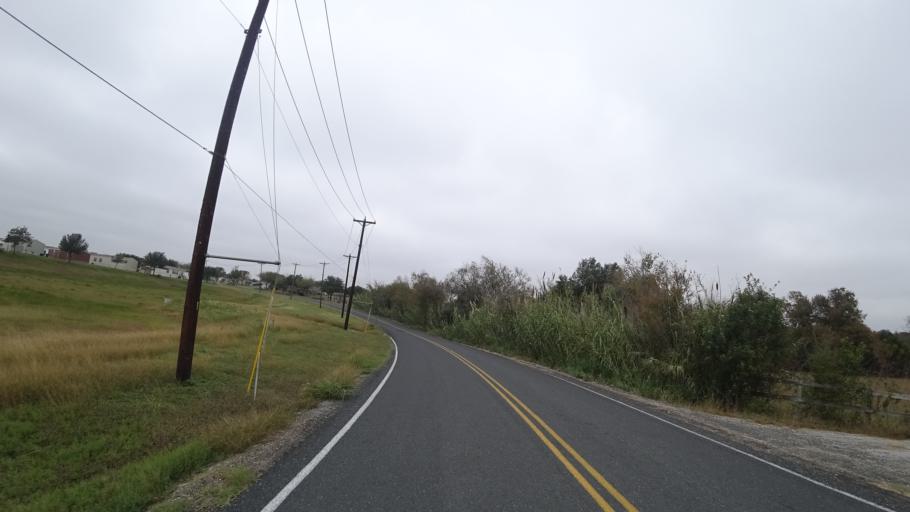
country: US
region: Texas
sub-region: Travis County
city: Pflugerville
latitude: 30.4101
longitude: -97.6031
